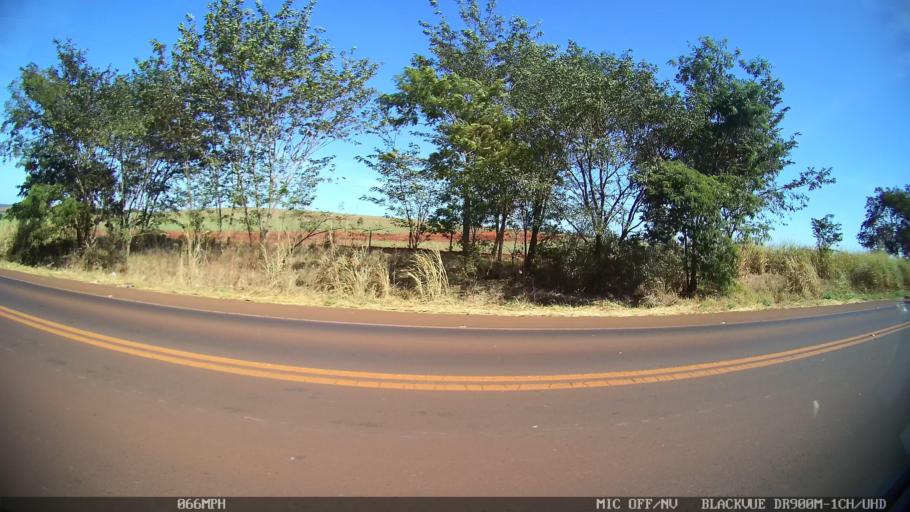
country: BR
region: Sao Paulo
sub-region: Sao Joaquim Da Barra
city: Sao Joaquim da Barra
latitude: -20.5266
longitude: -47.8368
